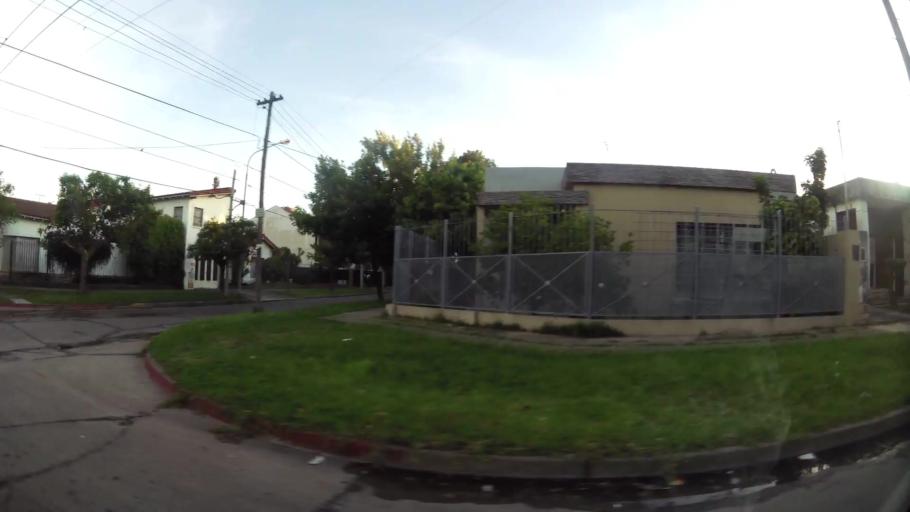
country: AR
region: Buenos Aires
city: Ituzaingo
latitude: -34.6509
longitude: -58.6510
